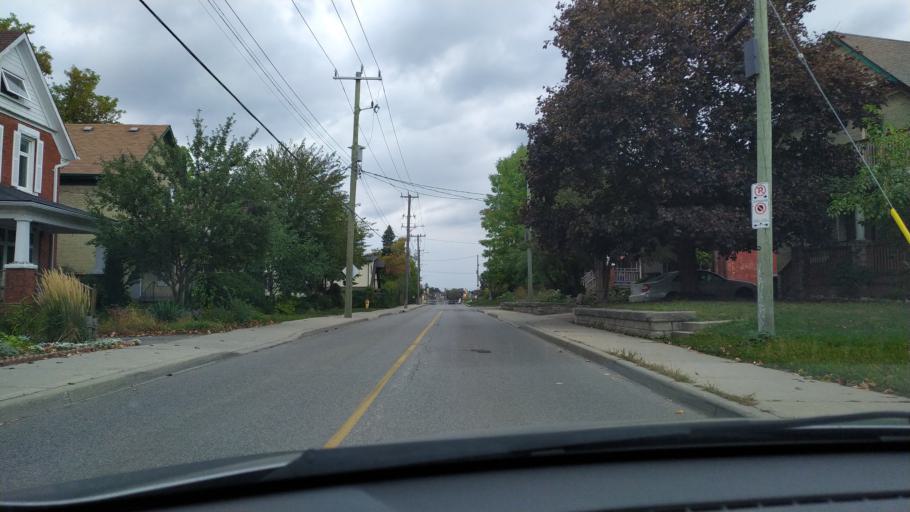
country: CA
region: Ontario
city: Waterloo
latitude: 43.4565
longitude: -80.4819
